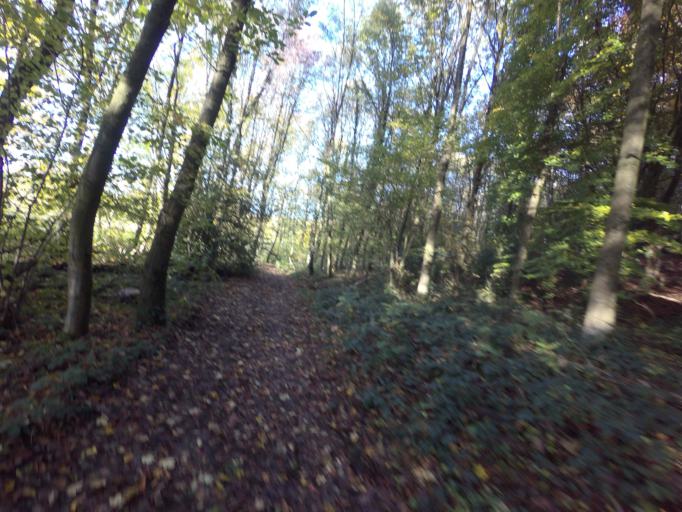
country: BE
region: Wallonia
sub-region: Province de Liege
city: Plombieres
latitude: 50.7770
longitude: 5.9371
